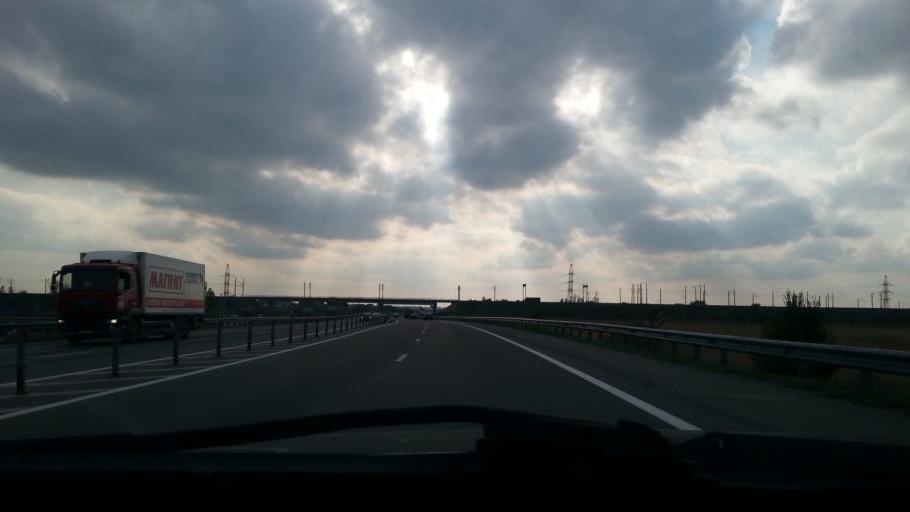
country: RU
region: Rostov
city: Bataysk
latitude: 47.1469
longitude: 39.7031
